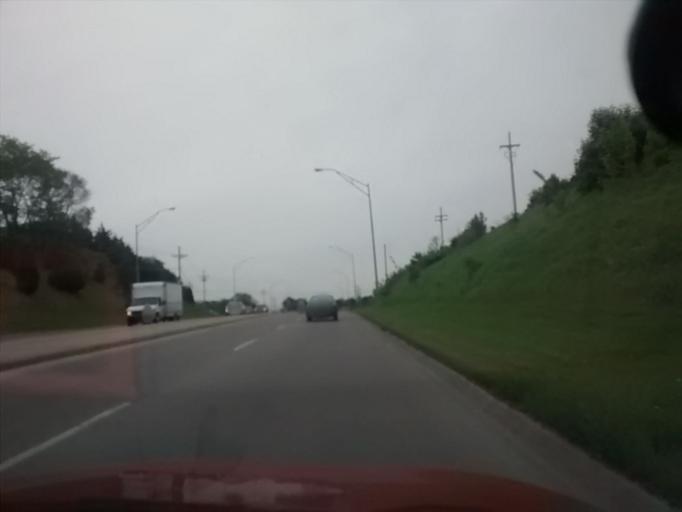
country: US
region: Nebraska
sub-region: Sarpy County
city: Offutt Air Force Base
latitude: 41.1605
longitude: -95.9583
